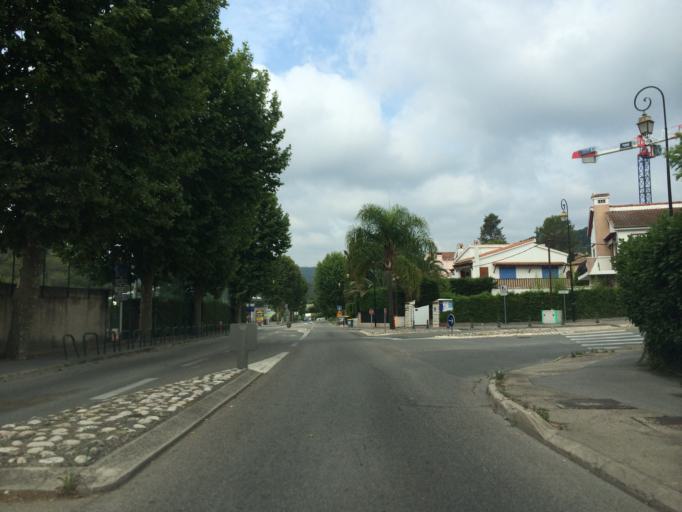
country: FR
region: Provence-Alpes-Cote d'Azur
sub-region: Departement des Alpes-Maritimes
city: La Colle-sur-Loup
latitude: 43.6858
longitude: 7.1001
